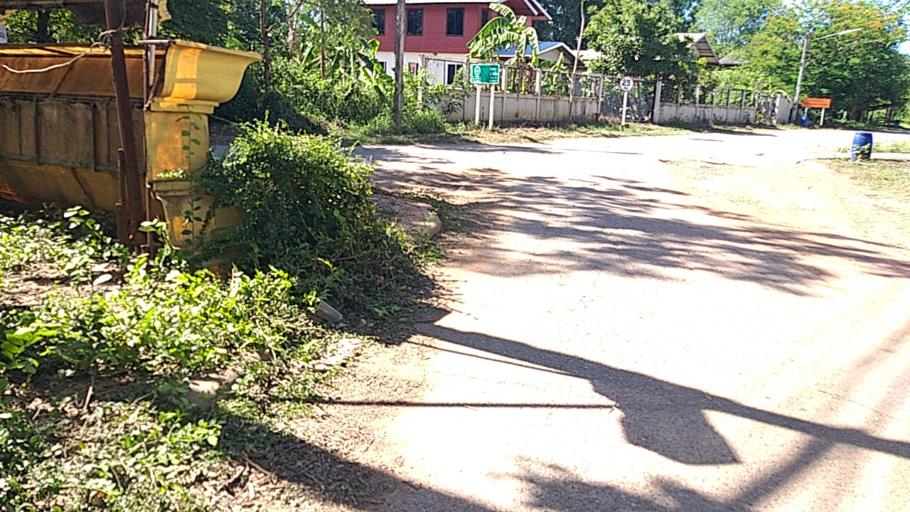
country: TH
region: Chaiyaphum
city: Ban Thaen
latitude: 16.4050
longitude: 102.3527
